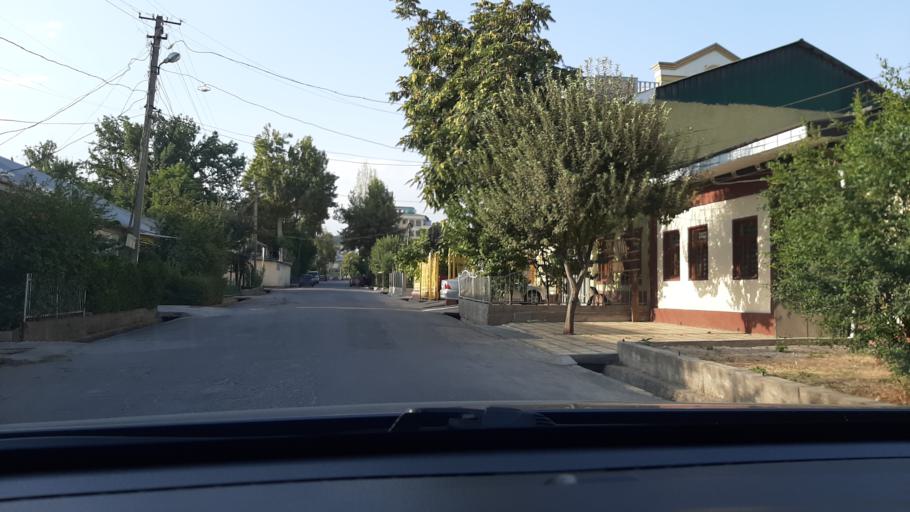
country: TJ
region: Dushanbe
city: Dushanbe
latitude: 38.5642
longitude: 68.8118
